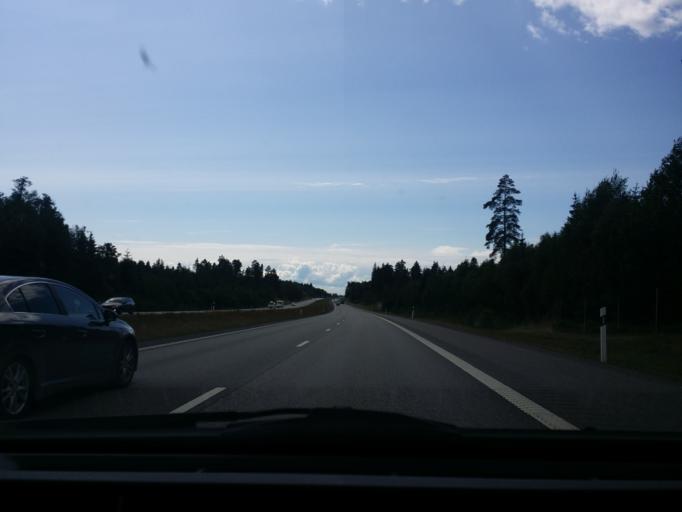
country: SE
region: OErebro
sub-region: Lindesbergs Kommun
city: Fellingsbro
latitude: 59.3658
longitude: 15.5760
